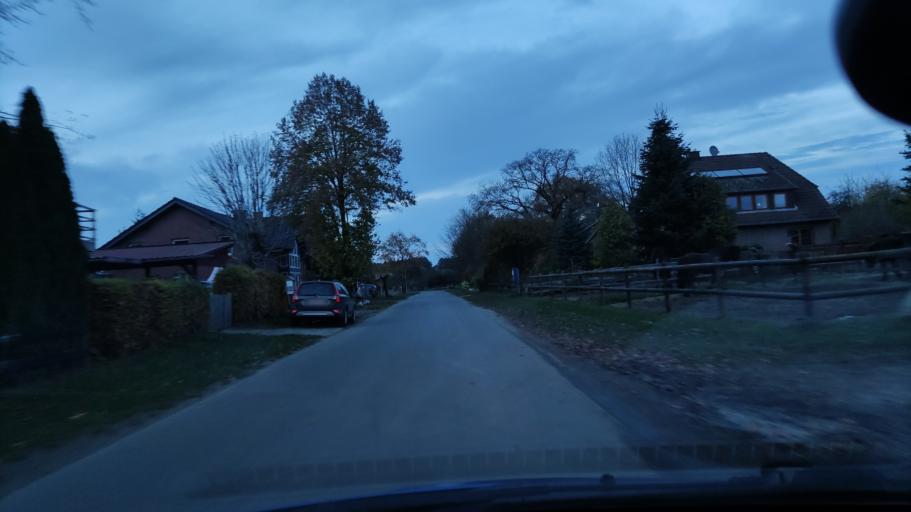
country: DE
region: Lower Saxony
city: Egestorf
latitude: 53.1469
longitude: 10.0331
